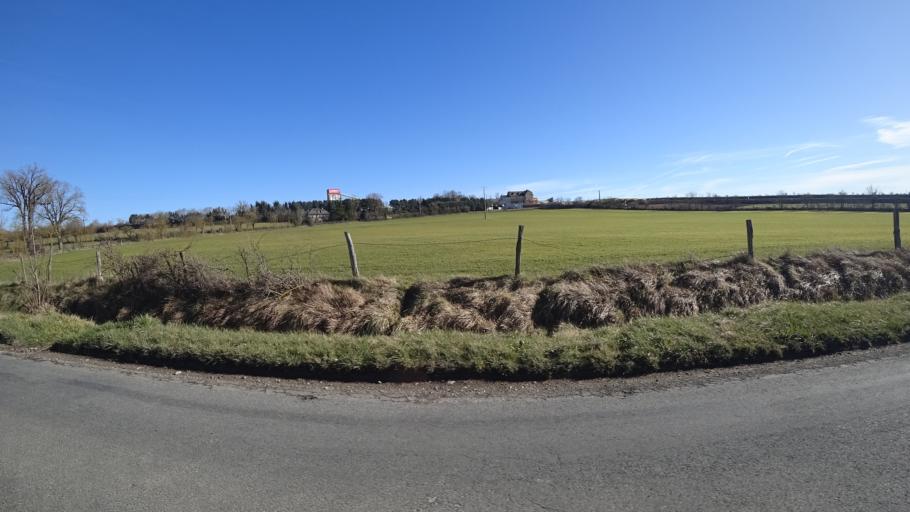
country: FR
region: Midi-Pyrenees
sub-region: Departement de l'Aveyron
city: Sebazac-Concoures
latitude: 44.3862
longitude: 2.5906
